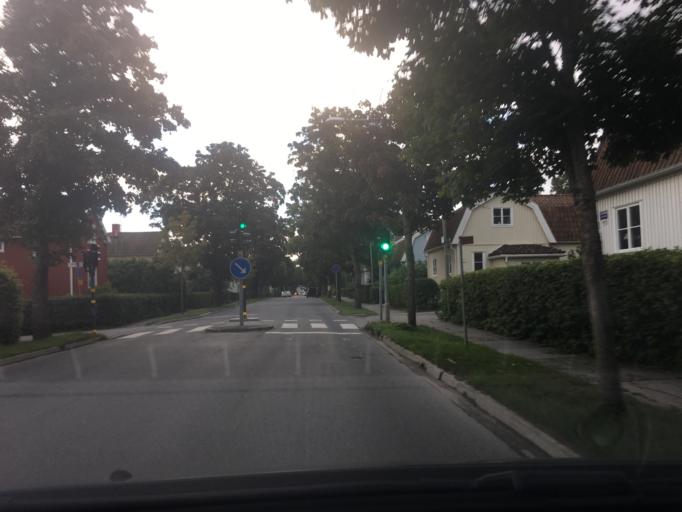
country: SE
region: Stockholm
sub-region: Stockholms Kommun
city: Bromma
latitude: 59.3306
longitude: 17.9368
